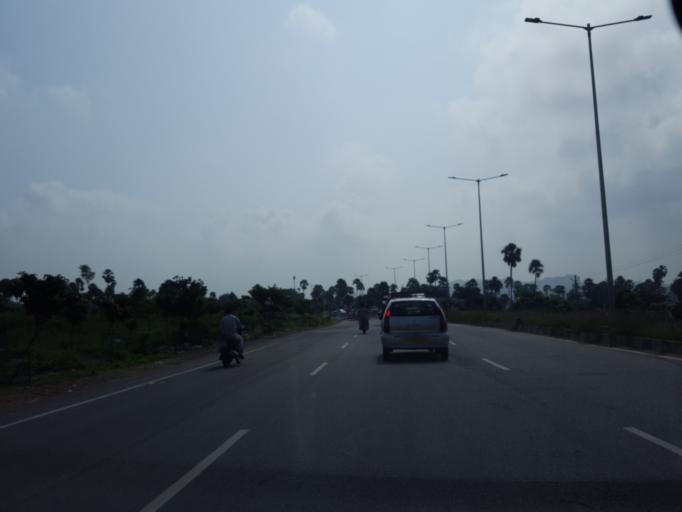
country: IN
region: Telangana
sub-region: Rangareddi
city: Ghatkesar
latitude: 17.3069
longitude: 78.7038
